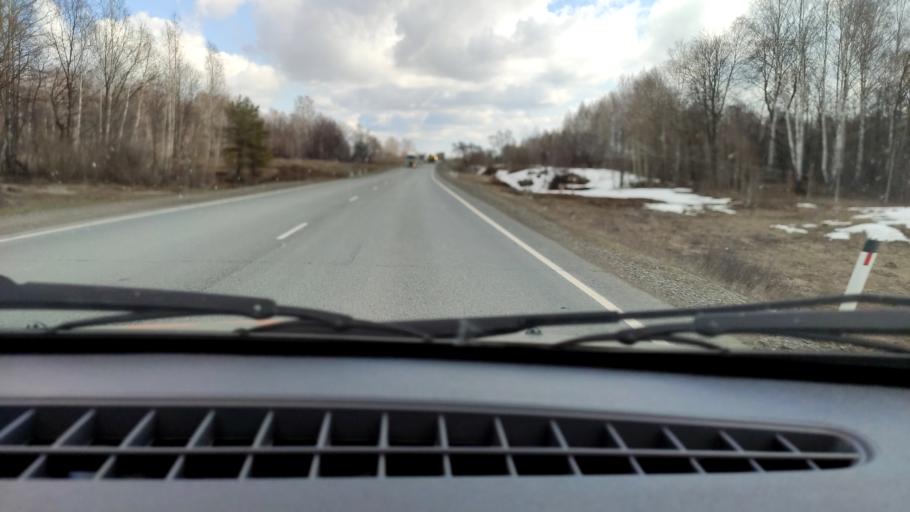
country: RU
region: Bashkortostan
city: Kudeyevskiy
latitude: 54.8162
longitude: 56.7039
